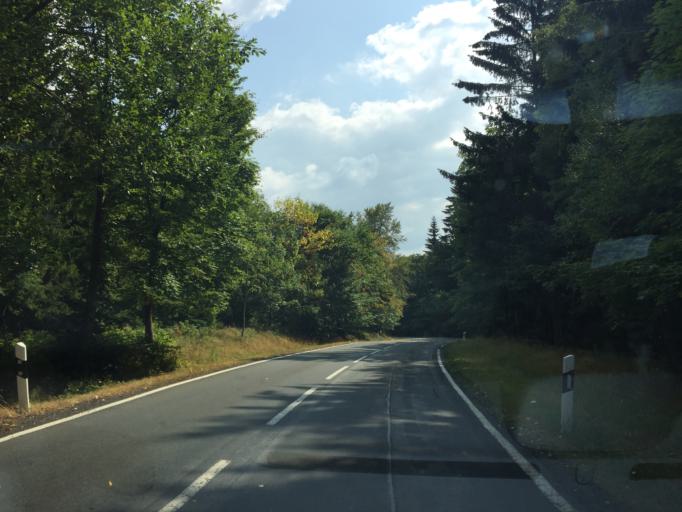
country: DE
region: Saxony-Anhalt
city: Benneckenstein
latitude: 51.6638
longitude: 10.6894
